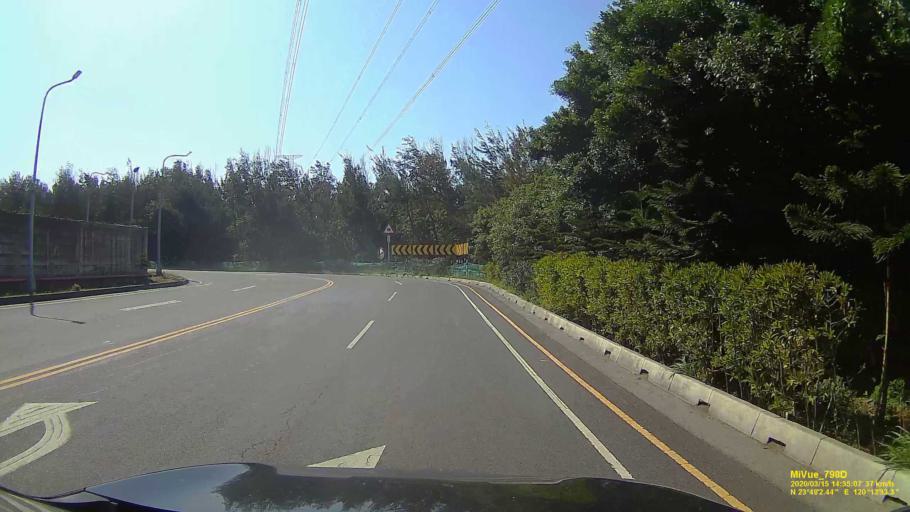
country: TW
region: Taiwan
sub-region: Yunlin
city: Douliu
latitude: 23.8174
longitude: 120.2257
